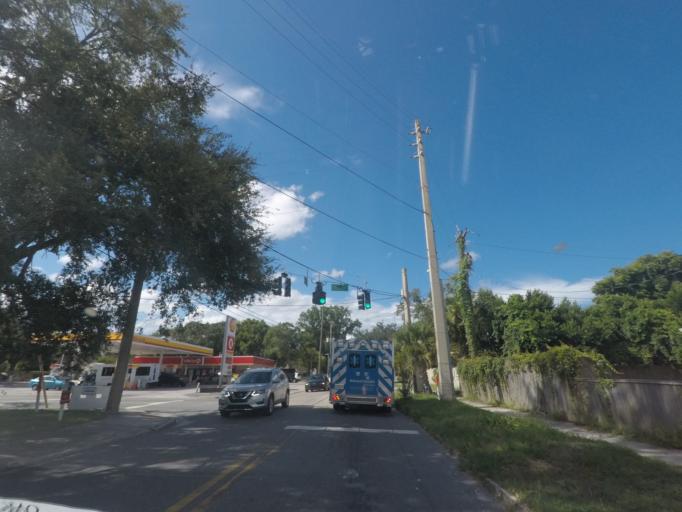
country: US
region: Florida
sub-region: Orange County
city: Fairview Shores
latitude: 28.5821
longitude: -81.3731
